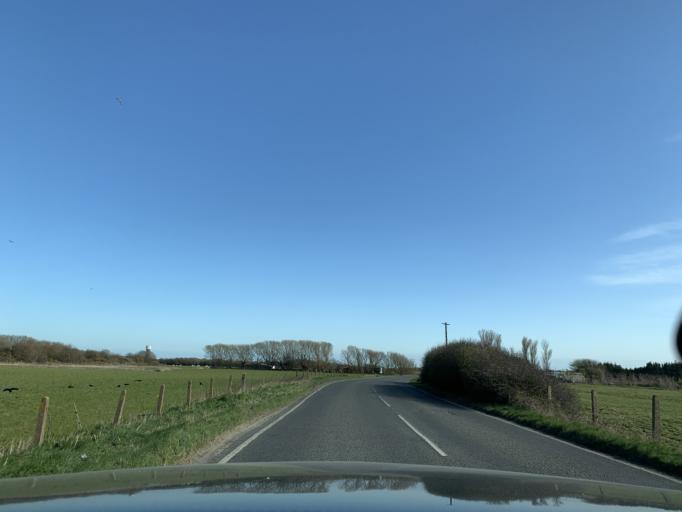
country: GB
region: England
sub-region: Kent
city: Lydd
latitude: 50.9452
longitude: 0.9258
